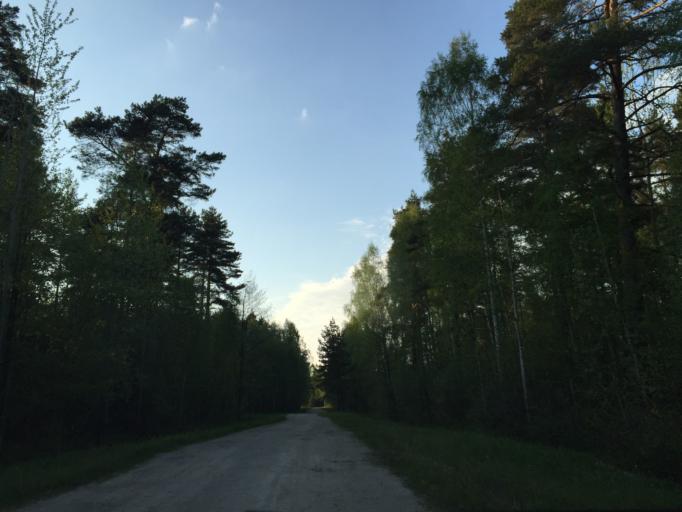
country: LV
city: Tireli
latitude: 56.8889
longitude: 23.6898
